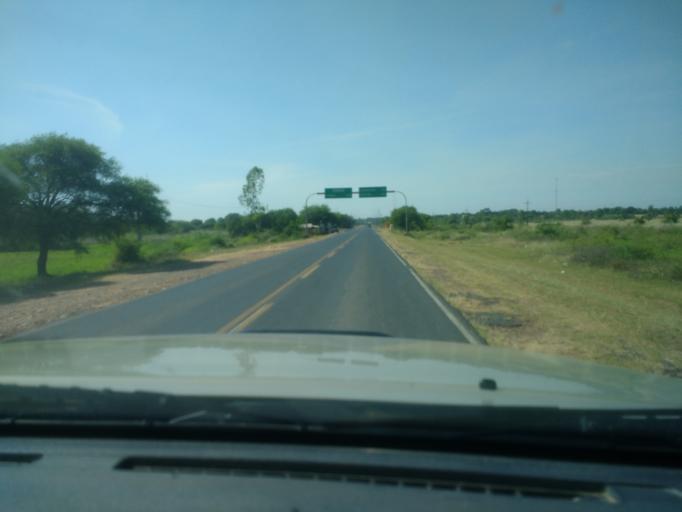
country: PY
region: Presidente Hayes
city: Benjamin Aceval
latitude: -24.9432
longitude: -57.5537
